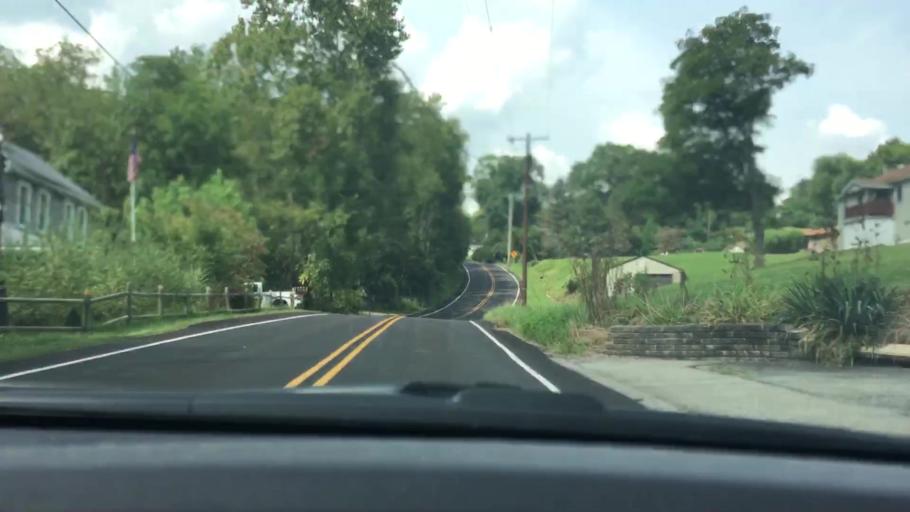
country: US
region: Pennsylvania
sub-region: Allegheny County
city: Versailles
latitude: 40.2916
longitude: -79.8388
